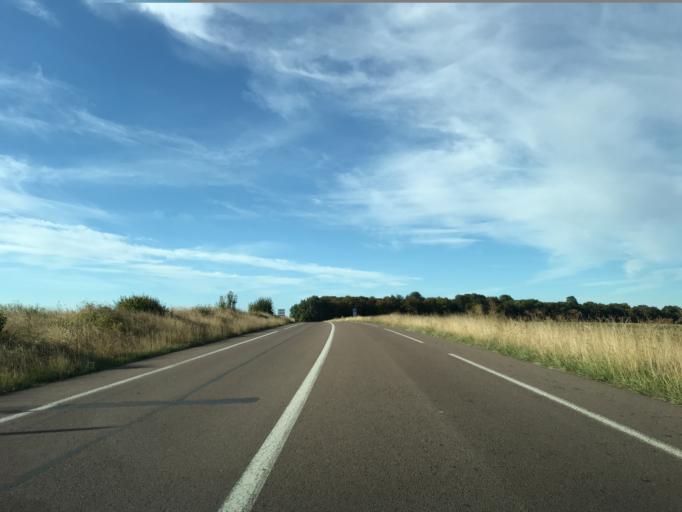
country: FR
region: Champagne-Ardenne
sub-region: Departement de la Marne
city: Chatillon-sur-Marne
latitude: 49.1523
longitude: 3.7158
